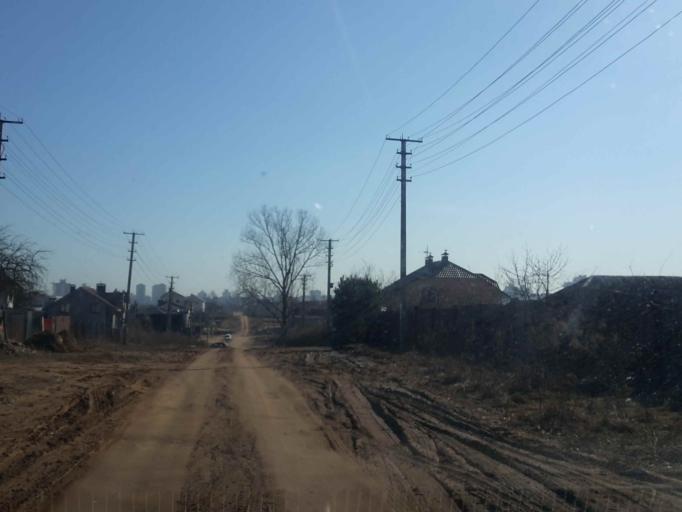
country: BY
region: Minsk
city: Zhdanovichy
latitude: 53.9250
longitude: 27.4018
